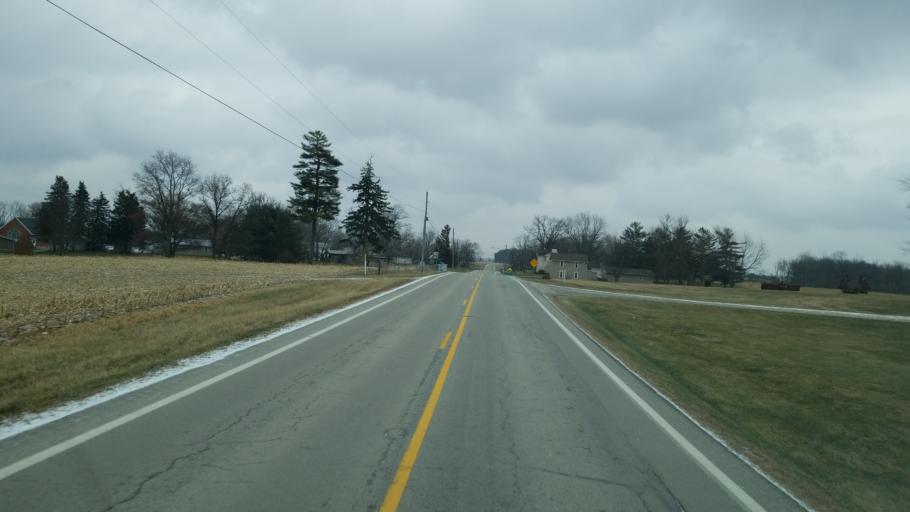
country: US
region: Ohio
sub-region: Wyandot County
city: Upper Sandusky
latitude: 40.7385
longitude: -83.2193
